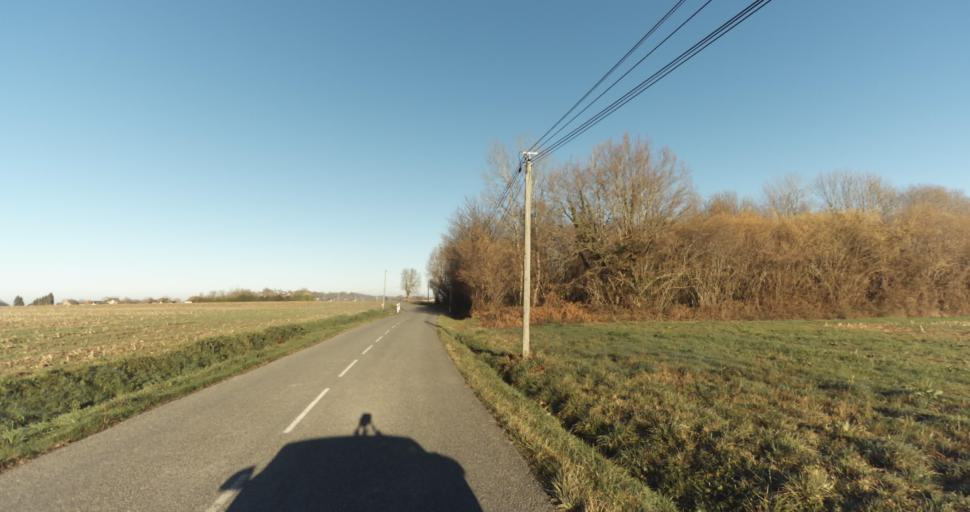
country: FR
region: Aquitaine
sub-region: Departement des Pyrenees-Atlantiques
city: Ousse
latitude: 43.3144
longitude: -0.2373
